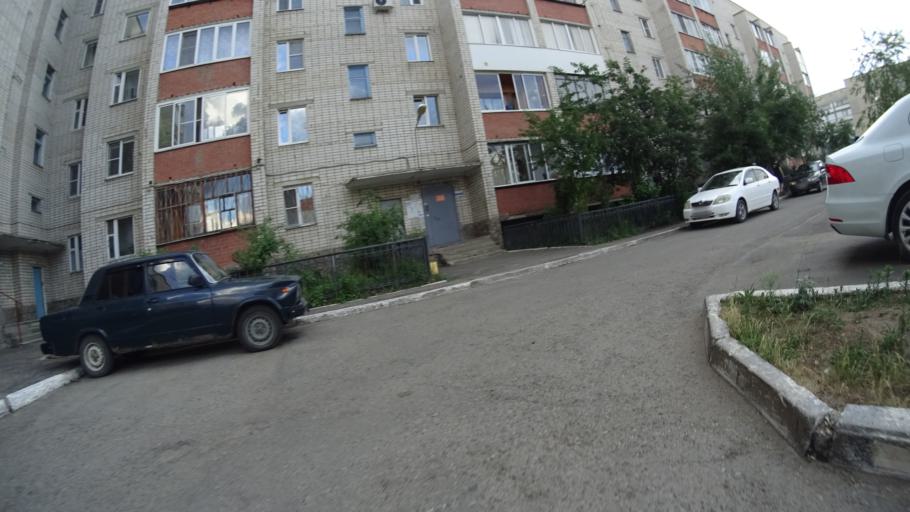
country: RU
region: Chelyabinsk
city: Troitsk
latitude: 54.0721
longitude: 61.5337
